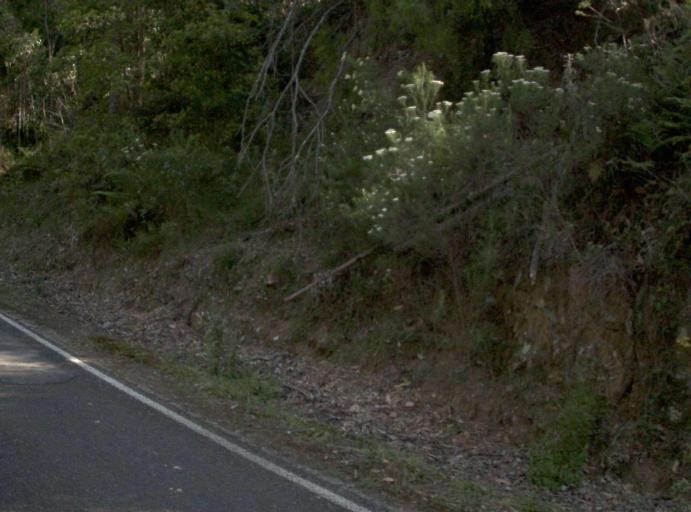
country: AU
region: Victoria
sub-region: East Gippsland
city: Lakes Entrance
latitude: -37.6443
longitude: 148.4809
